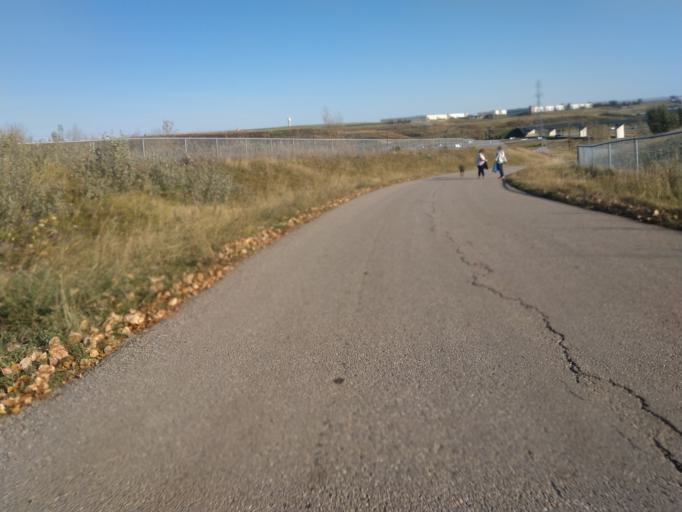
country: CA
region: Alberta
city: Calgary
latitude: 51.1286
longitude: -114.0513
